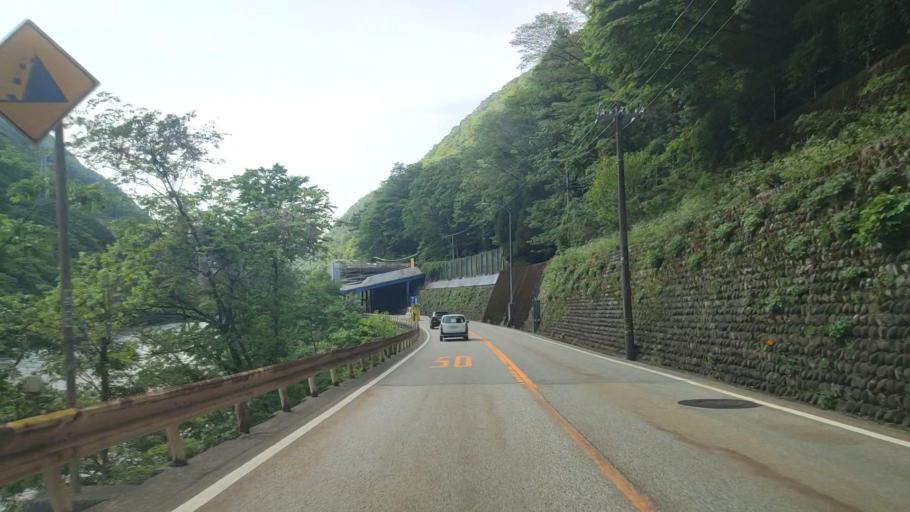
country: JP
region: Toyama
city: Yatsuomachi-higashikumisaka
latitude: 36.4118
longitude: 137.2921
